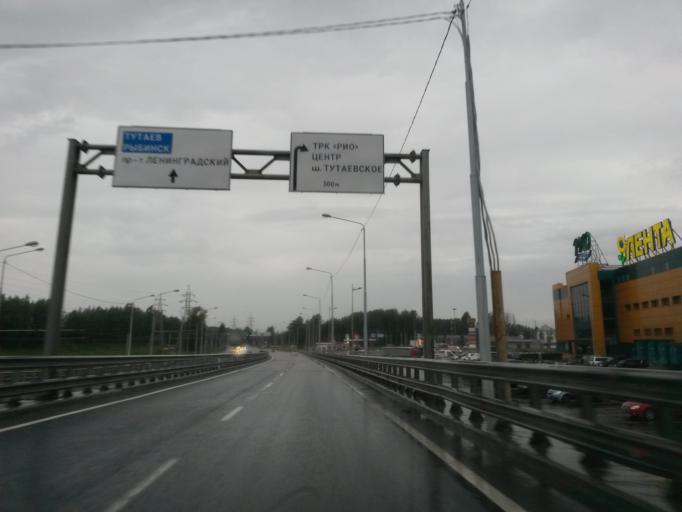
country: RU
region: Jaroslavl
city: Yaroslavl
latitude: 57.6696
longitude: 39.8370
